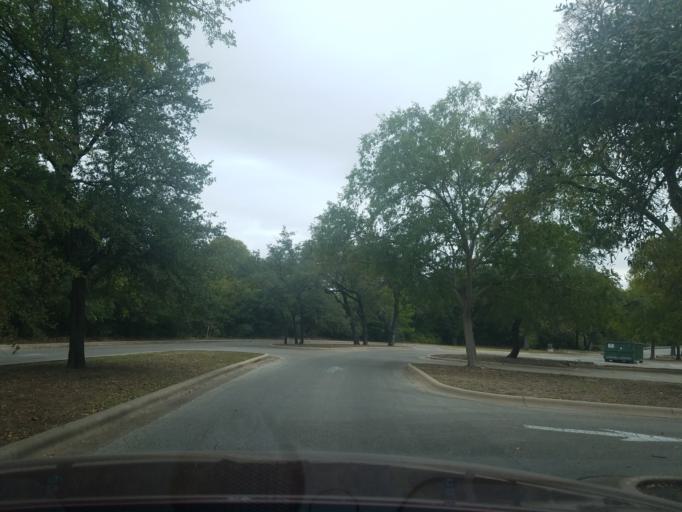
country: US
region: Texas
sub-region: Williamson County
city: Anderson Mill
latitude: 30.4690
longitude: -97.8103
